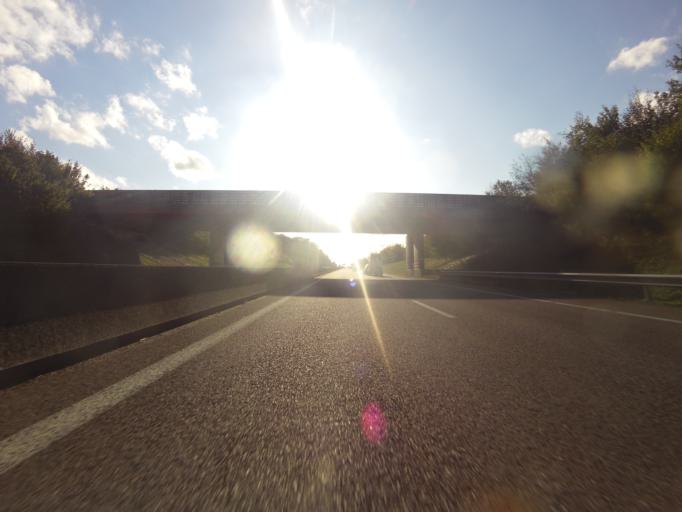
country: FR
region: Picardie
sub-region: Departement de la Somme
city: Saleux
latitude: 49.8708
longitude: 2.1929
